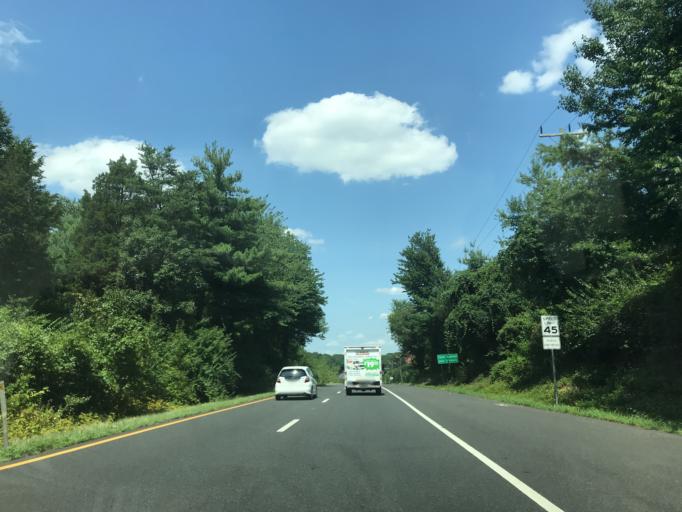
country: US
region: Maryland
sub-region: Prince George's County
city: College Park
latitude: 38.9892
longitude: -76.9538
